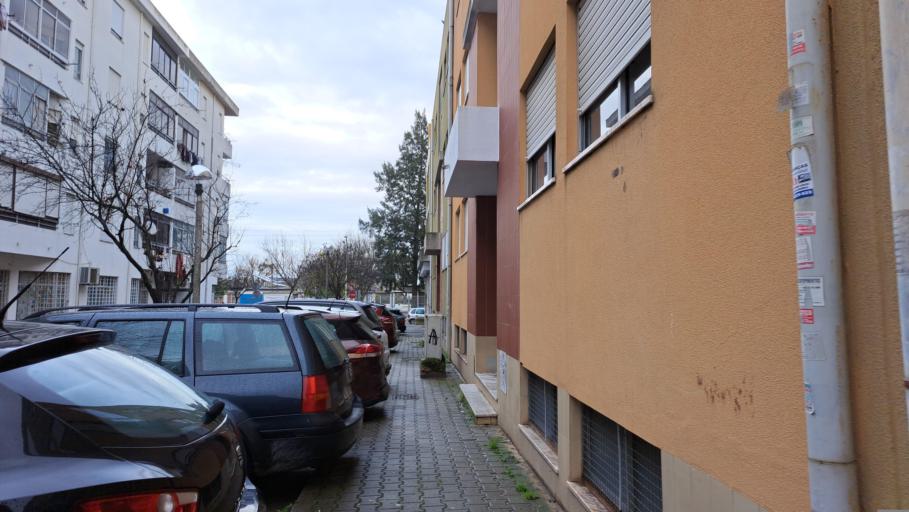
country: PT
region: Setubal
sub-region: Moita
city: Alhos Vedros
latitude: 38.6542
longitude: -9.0388
